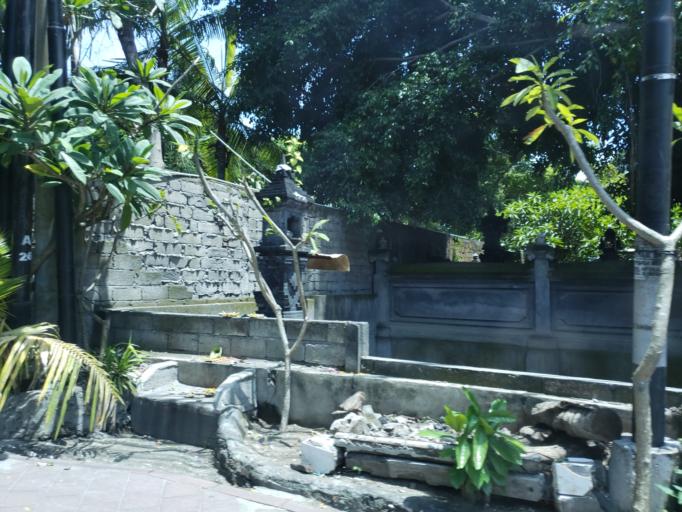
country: ID
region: Bali
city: Jimbaran
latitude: -8.7821
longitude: 115.1657
